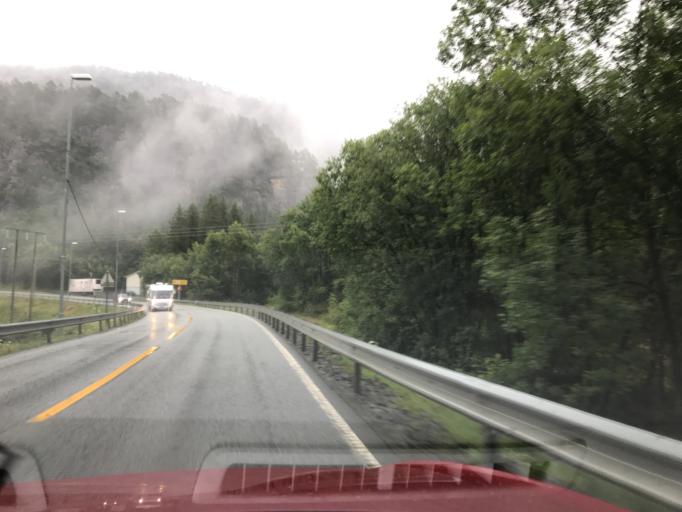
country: NO
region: Vest-Agder
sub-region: Flekkefjord
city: Flekkefjord
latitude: 58.3465
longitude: 6.6670
